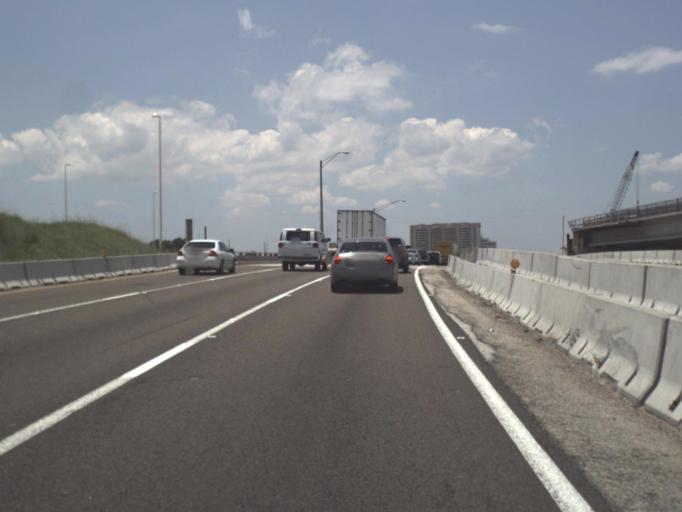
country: US
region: Florida
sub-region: Hillsborough County
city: Tampa
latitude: 27.9510
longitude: -82.5130
